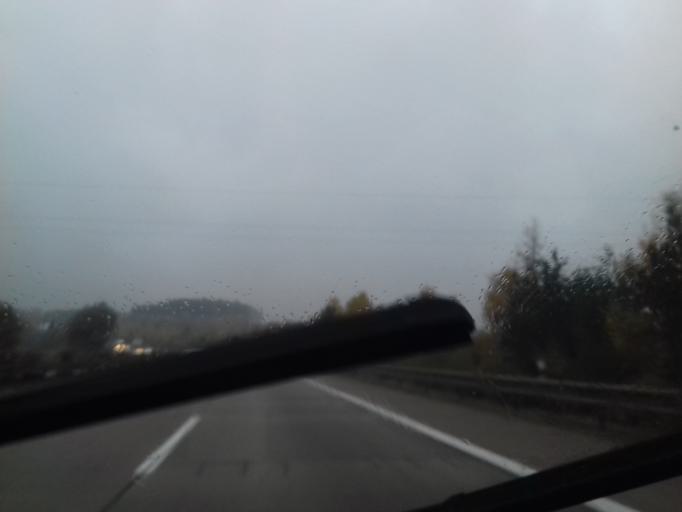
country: CZ
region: Vysocina
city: Heralec
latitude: 49.5150
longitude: 15.4591
